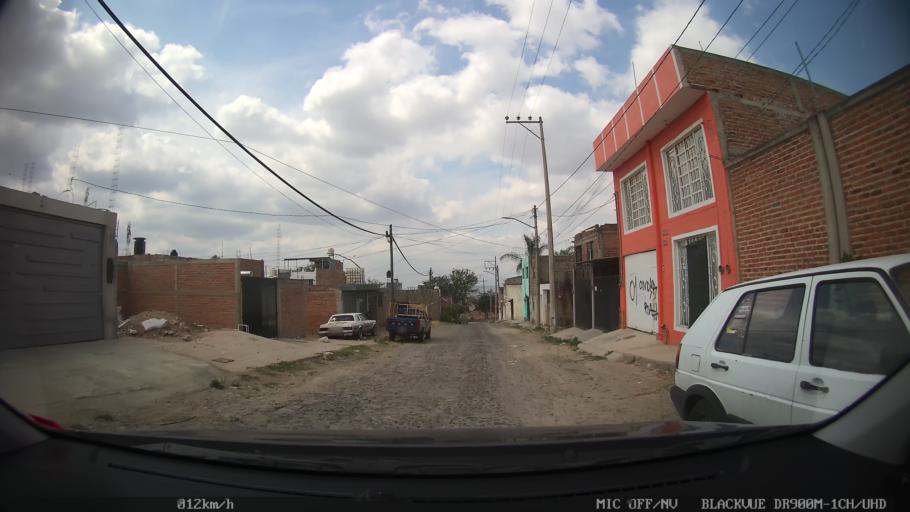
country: MX
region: Jalisco
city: Tonala
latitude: 20.6309
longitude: -103.2293
